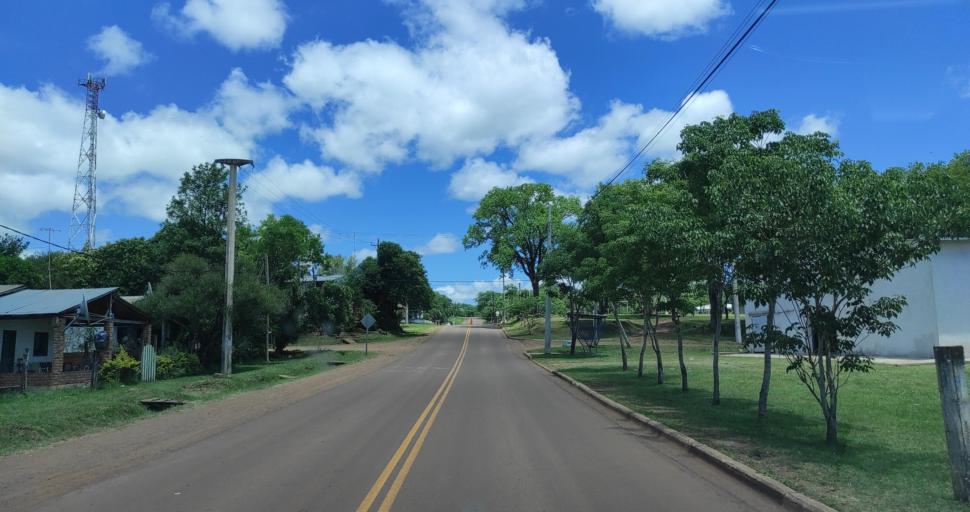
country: AR
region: Misiones
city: Cerro Cora
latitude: -27.5112
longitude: -55.6073
